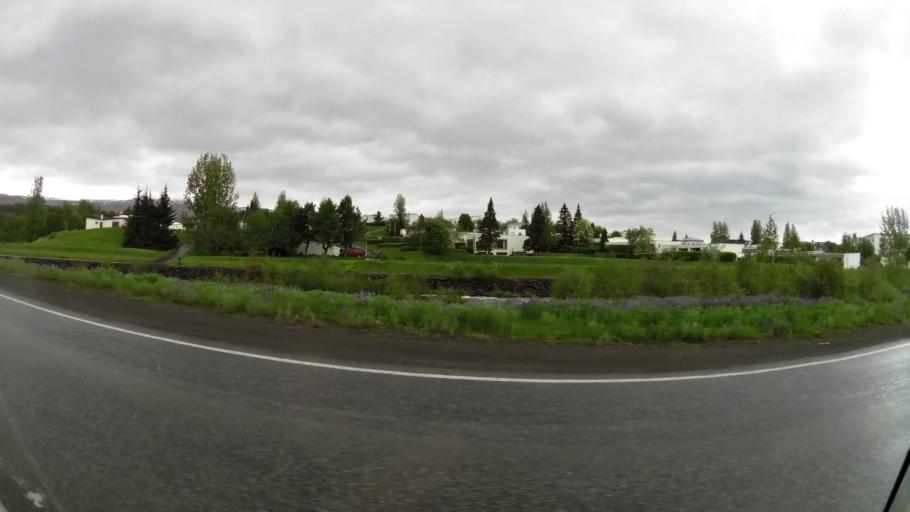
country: IS
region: Northeast
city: Akureyri
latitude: 65.6871
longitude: -18.1083
